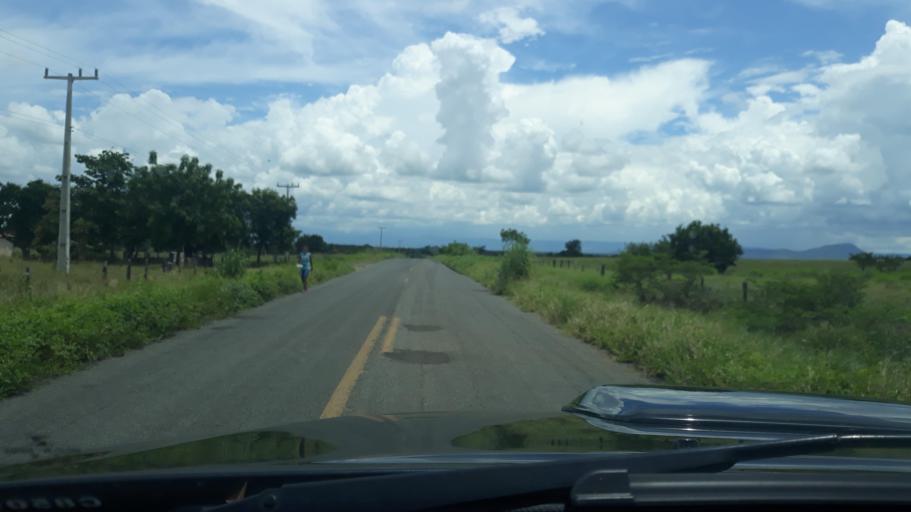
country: BR
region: Bahia
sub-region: Guanambi
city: Guanambi
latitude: -14.0634
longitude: -42.8774
